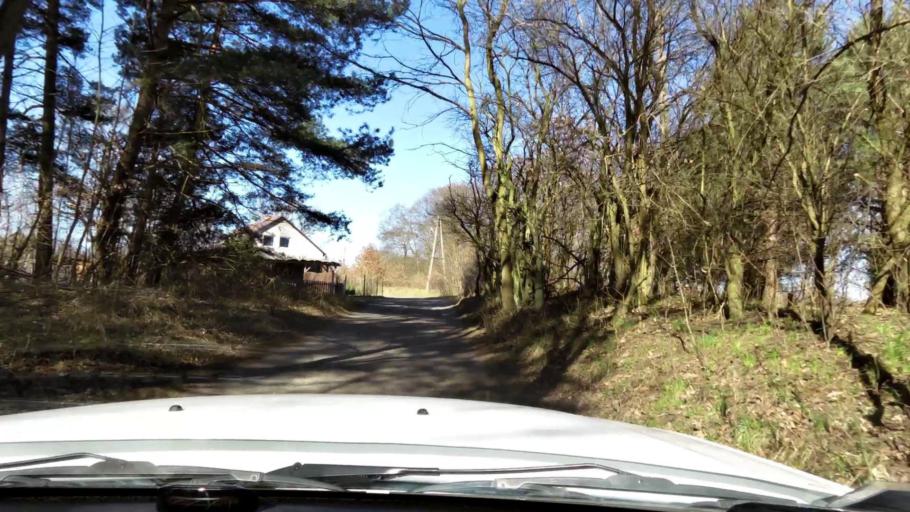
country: PL
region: West Pomeranian Voivodeship
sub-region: Powiat gryfinski
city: Gryfino
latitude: 53.2242
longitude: 14.5264
